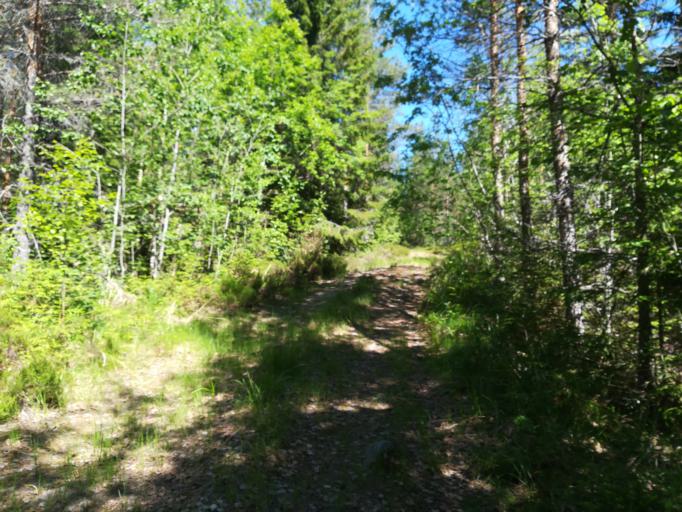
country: FI
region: Southern Savonia
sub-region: Mikkeli
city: Puumala
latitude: 61.6175
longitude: 28.1616
